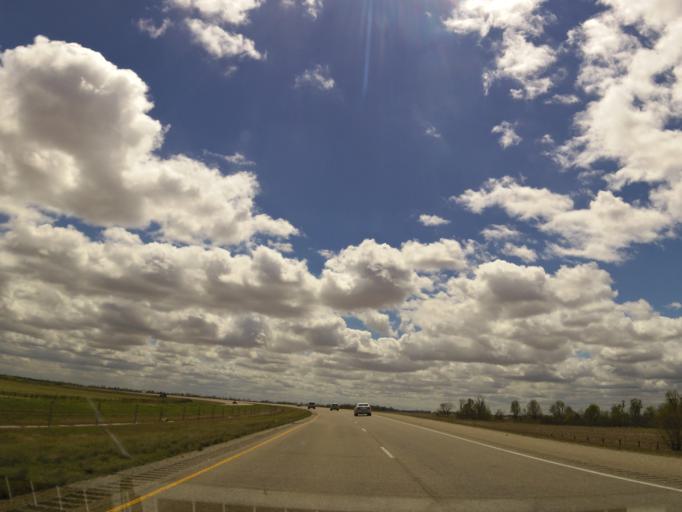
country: US
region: Arkansas
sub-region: Craighead County
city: Bay
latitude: 35.7200
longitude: -90.5801
